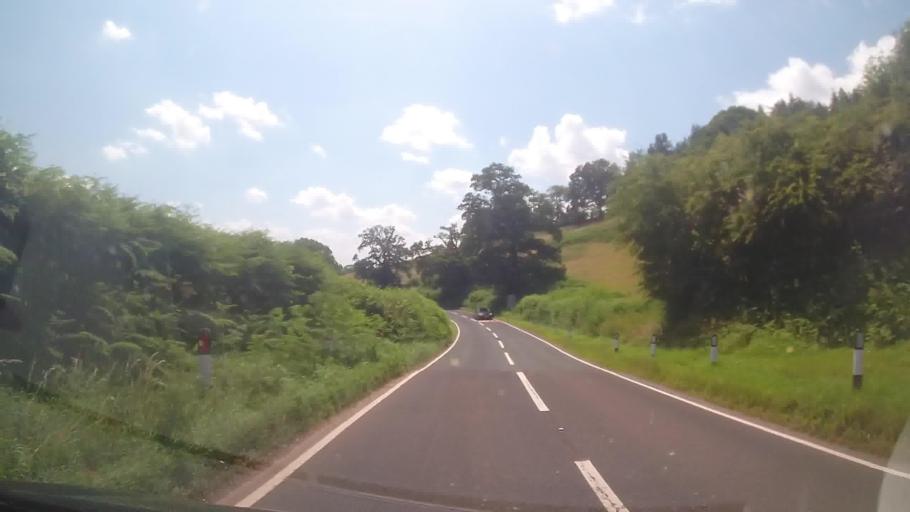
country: GB
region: England
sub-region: Herefordshire
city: Brockhampton
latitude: 51.9916
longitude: -2.5733
